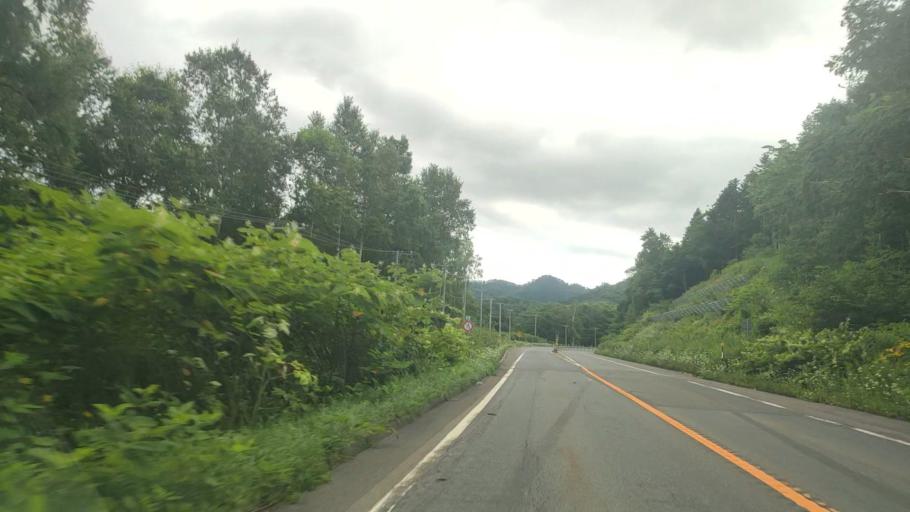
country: JP
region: Hokkaido
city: Niseko Town
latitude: 42.5998
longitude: 140.5809
